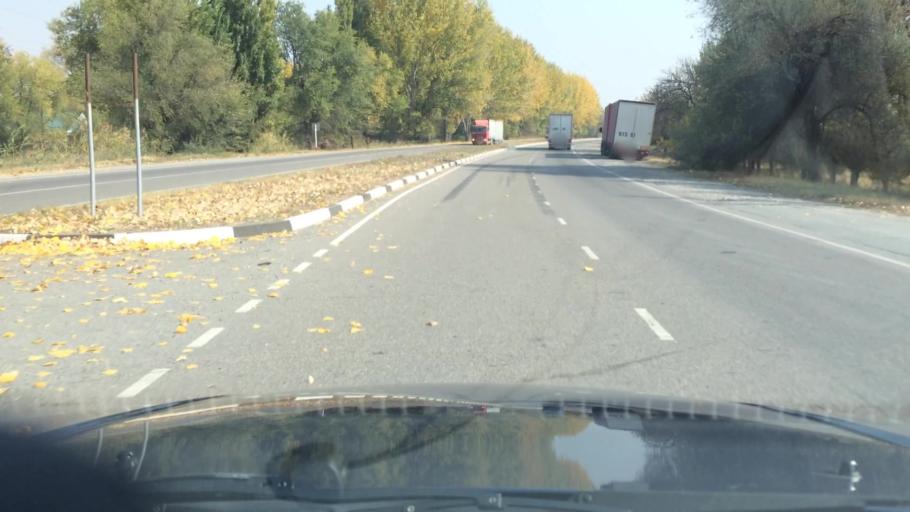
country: KG
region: Chuy
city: Kant
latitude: 42.9731
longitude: 74.8580
